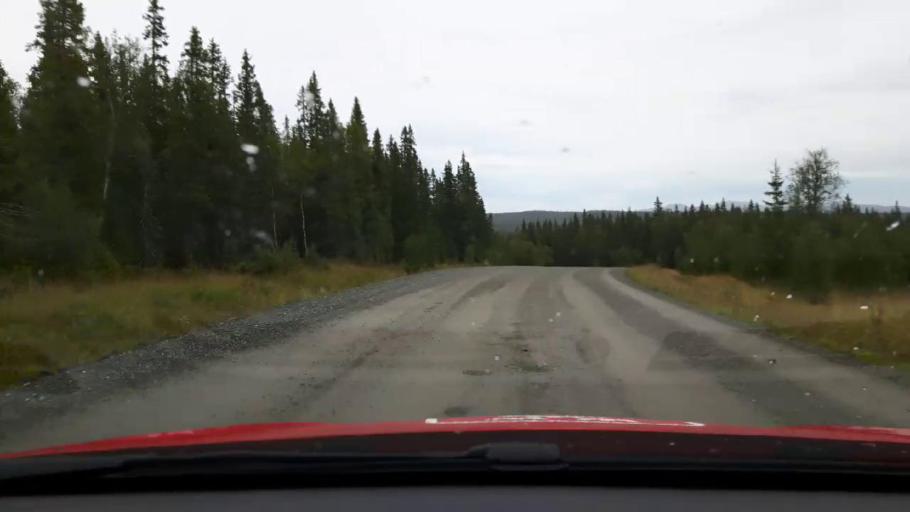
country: SE
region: Jaemtland
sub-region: Are Kommun
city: Are
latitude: 63.4698
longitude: 12.5812
